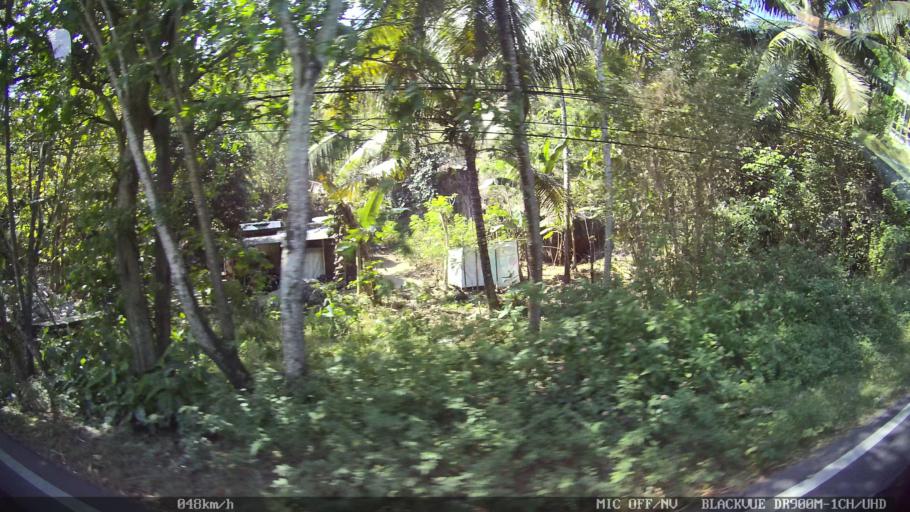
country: ID
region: Daerah Istimewa Yogyakarta
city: Pundong
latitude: -8.0172
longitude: 110.3237
